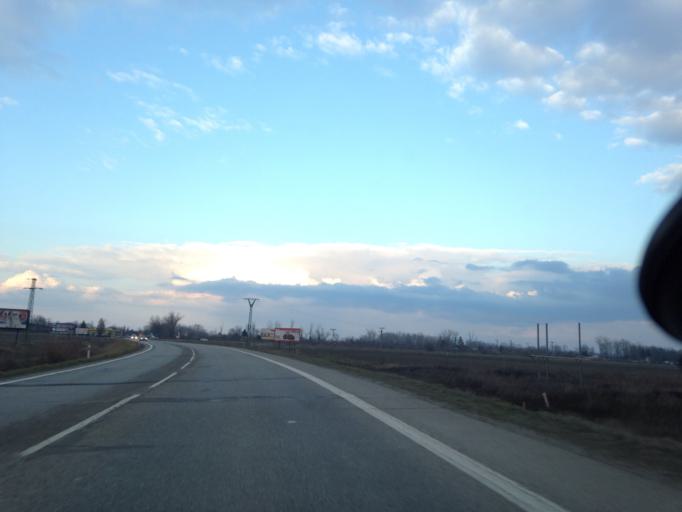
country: SK
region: Nitriansky
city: Komarno
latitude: 47.7639
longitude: 18.1515
